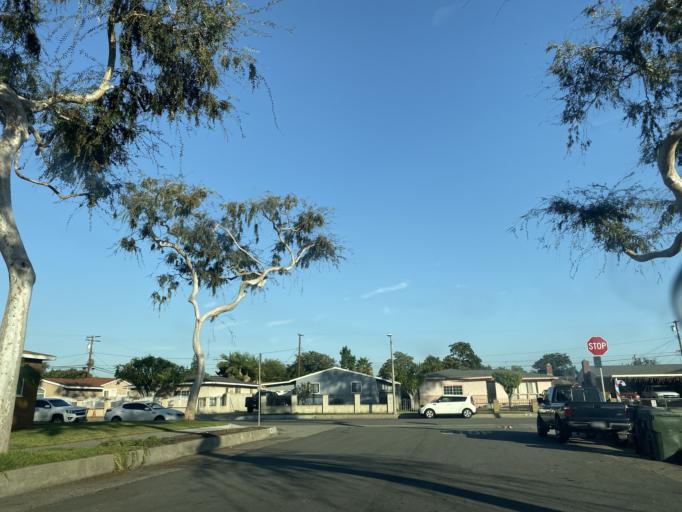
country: US
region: California
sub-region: Orange County
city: Fullerton
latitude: 33.8653
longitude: -117.9181
